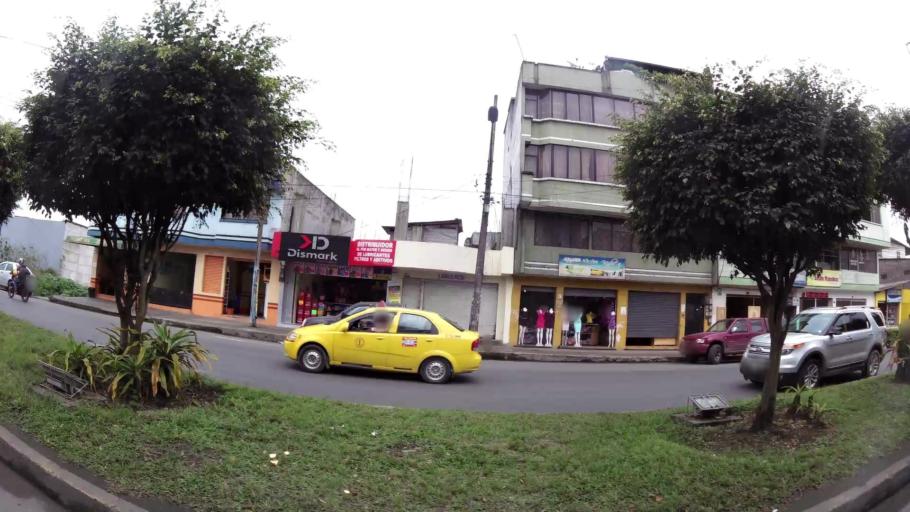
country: EC
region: Santo Domingo de los Tsachilas
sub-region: Canton Santo Domingo de los Colorados
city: Santo Domingo de los Colorados
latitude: -0.2510
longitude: -79.1757
